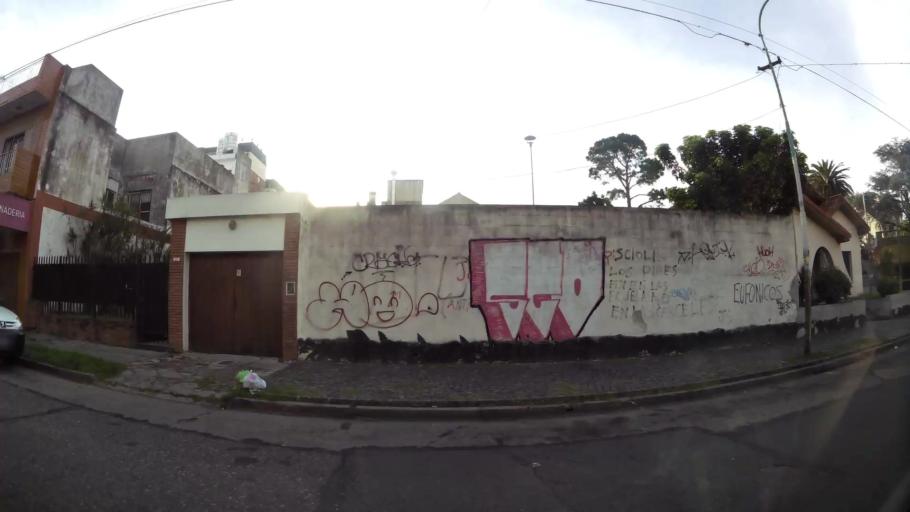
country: AR
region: Buenos Aires
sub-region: Partido de Moron
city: Moron
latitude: -34.6509
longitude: -58.6140
